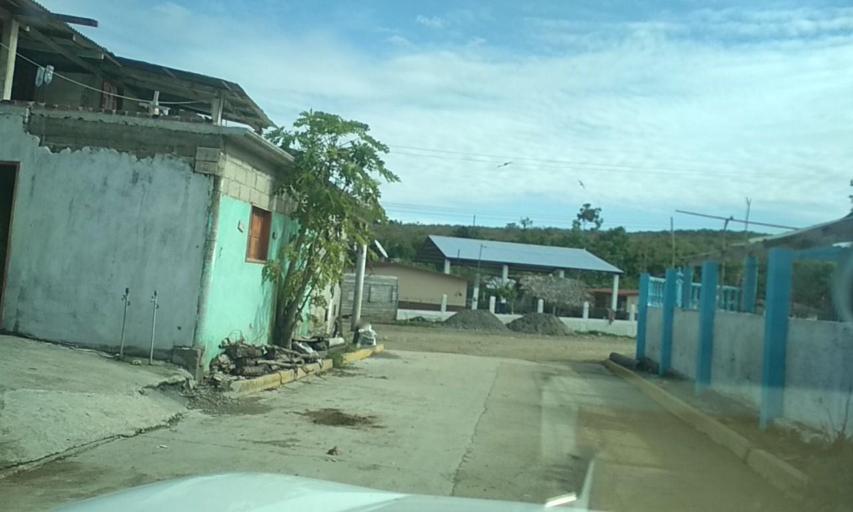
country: MX
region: Veracruz
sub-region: Papantla
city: Polutla
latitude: 20.5717
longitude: -97.1885
